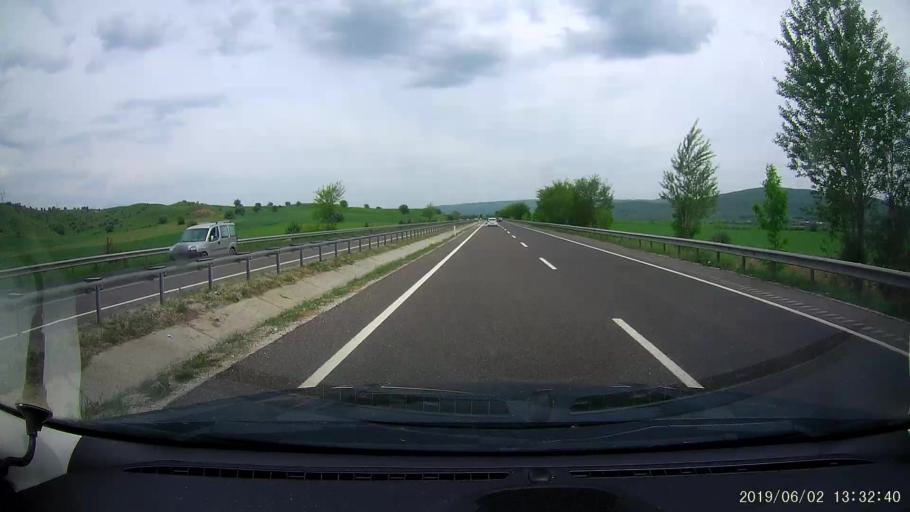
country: TR
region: Cankiri
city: Atkaracalar
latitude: 40.8015
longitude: 32.9926
